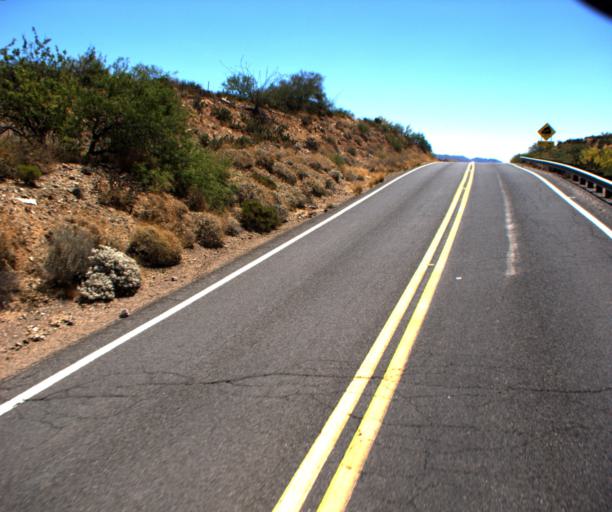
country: US
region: Arizona
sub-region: Pinal County
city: Superior
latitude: 33.1798
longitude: -111.0404
